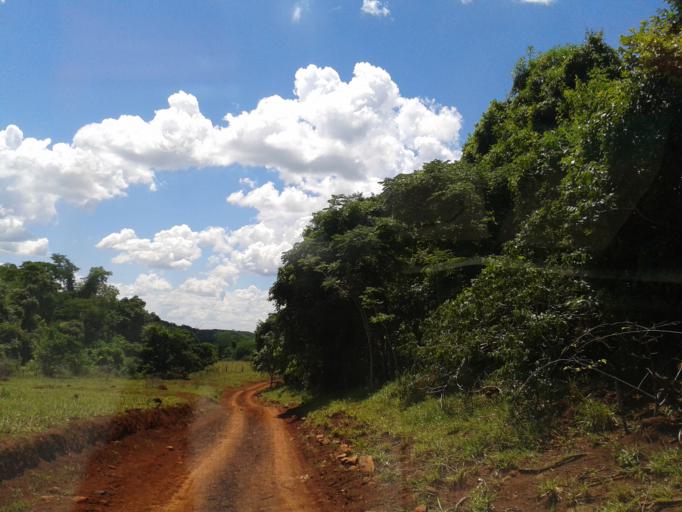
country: BR
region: Minas Gerais
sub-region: Centralina
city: Centralina
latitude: -18.6873
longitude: -49.1816
